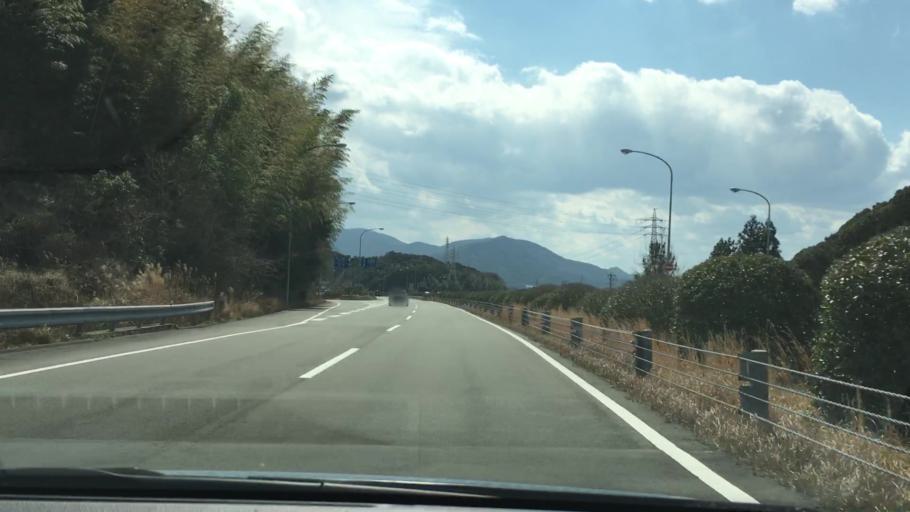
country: JP
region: Mie
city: Ise
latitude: 34.4876
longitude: 136.7573
